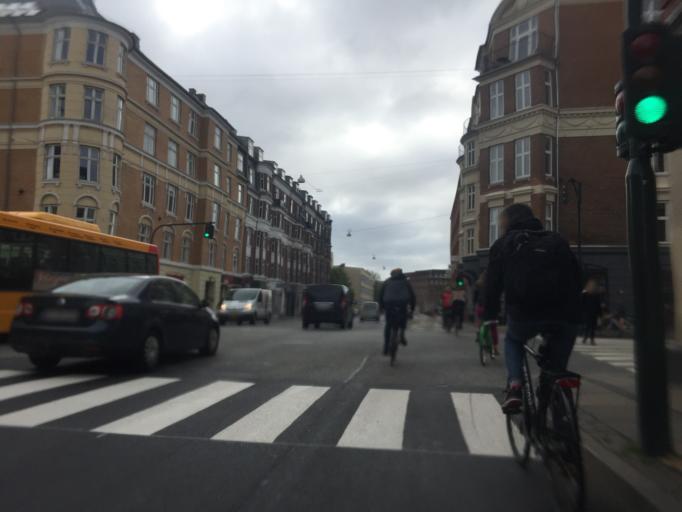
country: DK
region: Capital Region
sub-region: Frederiksberg Kommune
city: Frederiksberg
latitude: 55.6826
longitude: 12.5497
